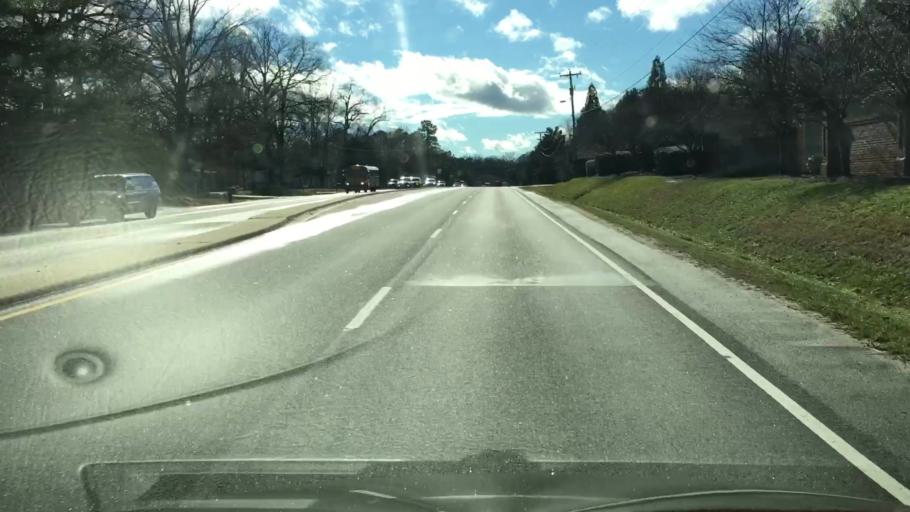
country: US
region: Virginia
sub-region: Chesterfield County
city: Bon Air
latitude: 37.5288
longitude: -77.5977
